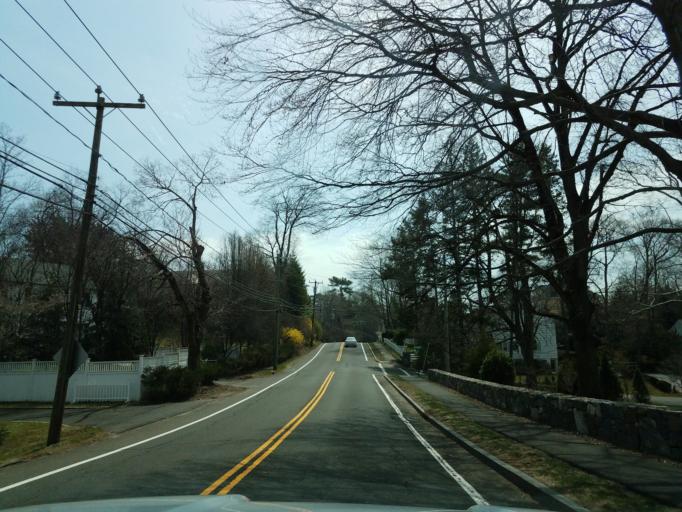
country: US
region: Connecticut
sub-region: Fairfield County
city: Greenwich
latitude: 41.0315
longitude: -73.6322
